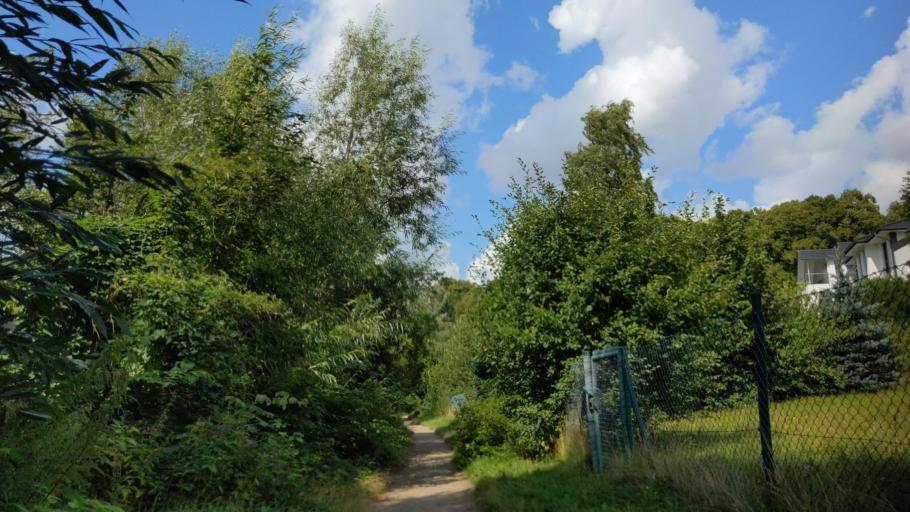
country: DE
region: Schleswig-Holstein
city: Reinfeld
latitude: 53.8341
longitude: 10.4860
